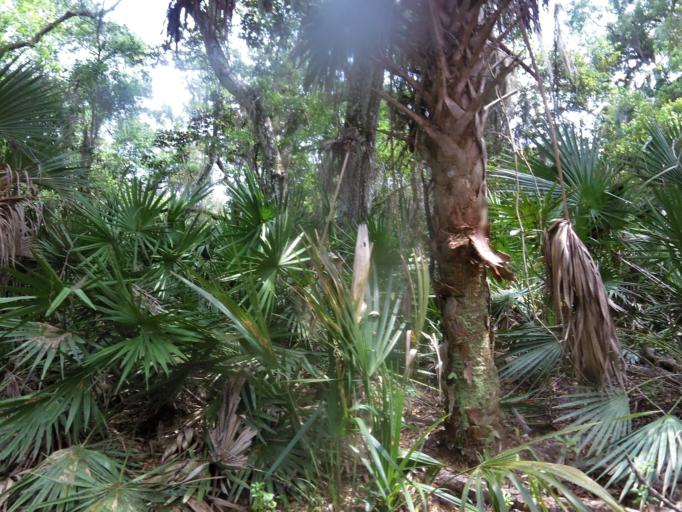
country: US
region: Florida
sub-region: Volusia County
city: Ormond-by-the-Sea
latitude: 29.3999
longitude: -81.1215
